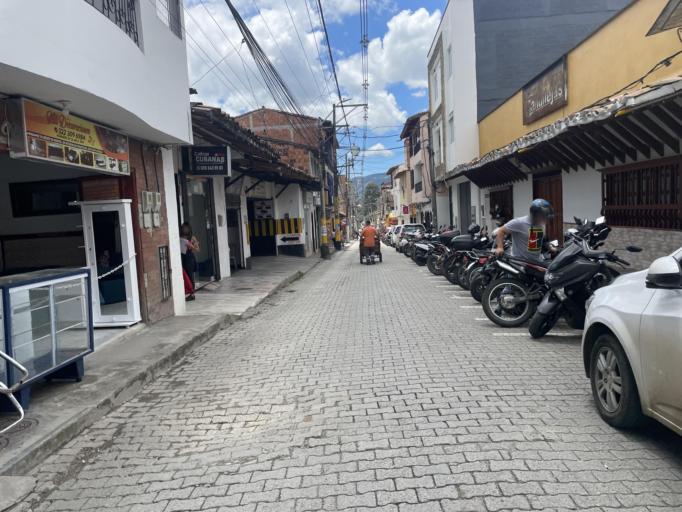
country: CO
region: Antioquia
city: La Ceja
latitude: 6.0320
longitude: -75.4316
